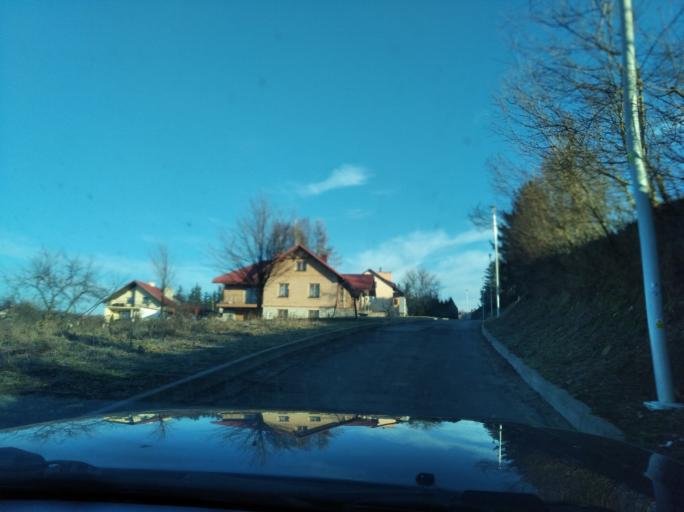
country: PL
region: Subcarpathian Voivodeship
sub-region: Powiat strzyzowski
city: Strzyzow
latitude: 49.8726
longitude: 21.8050
